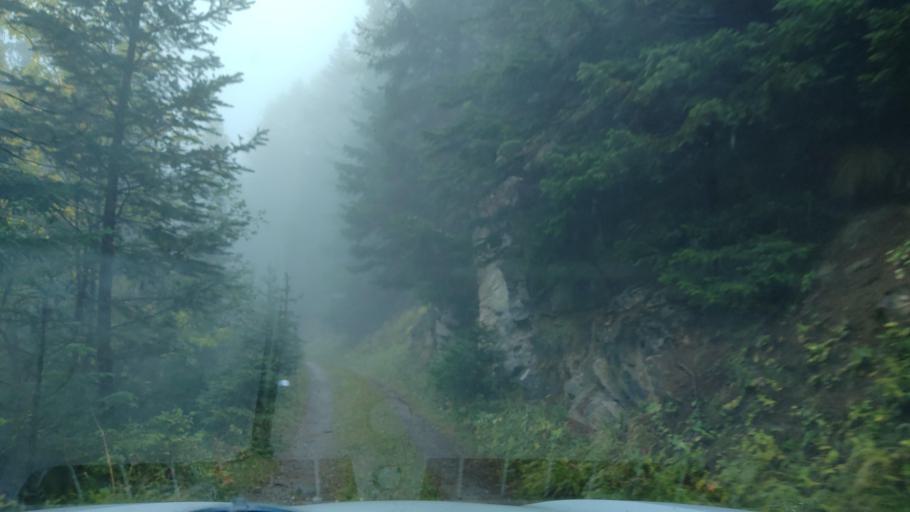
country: IT
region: Piedmont
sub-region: Provincia di Torino
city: Moncenisio
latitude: 45.2916
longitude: 6.8254
